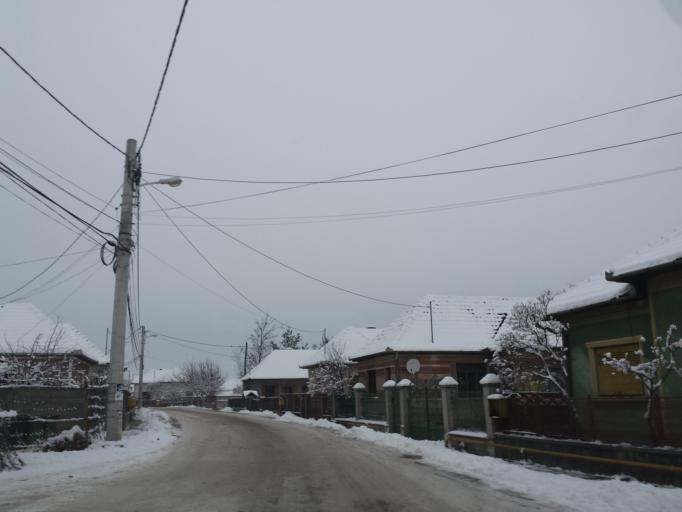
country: RO
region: Hunedoara
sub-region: Municipiul Deva
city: Cristur
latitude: 45.8245
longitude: 22.9417
